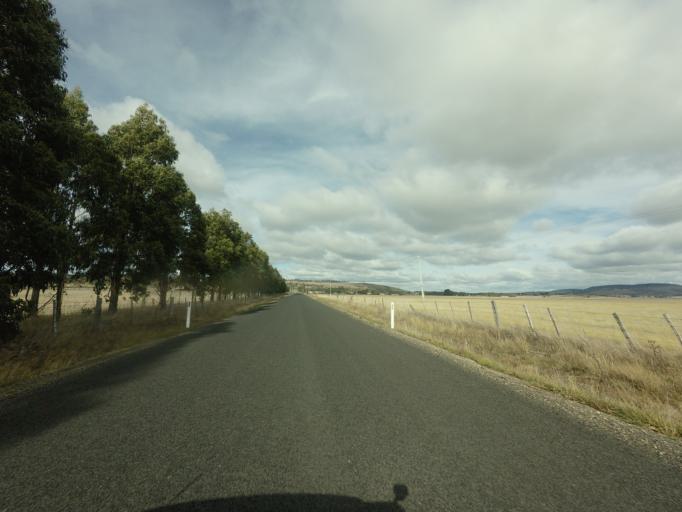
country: AU
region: Tasmania
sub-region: Brighton
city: Bridgewater
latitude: -42.3996
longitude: 147.3879
